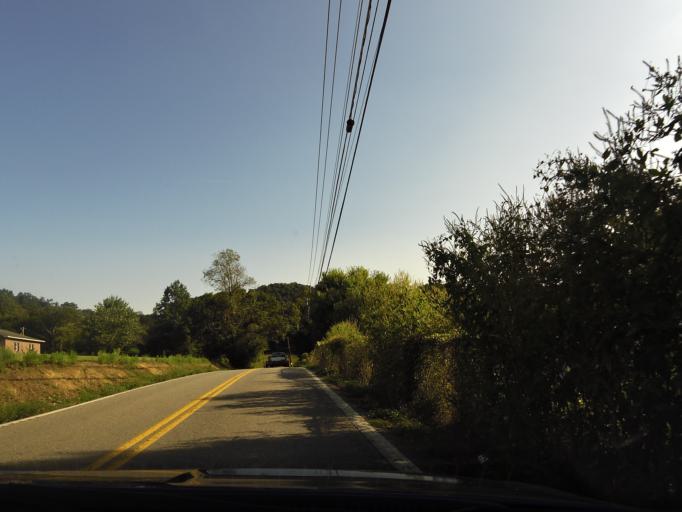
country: US
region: Tennessee
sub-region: Union County
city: Maynardville
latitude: 36.2604
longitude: -83.7690
